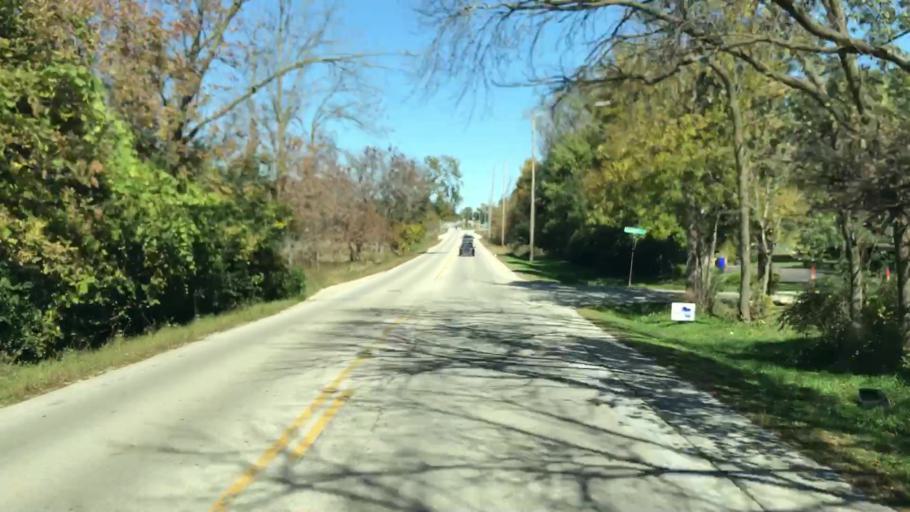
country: US
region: Wisconsin
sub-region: Waukesha County
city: Brookfield
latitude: 43.0559
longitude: -88.1664
